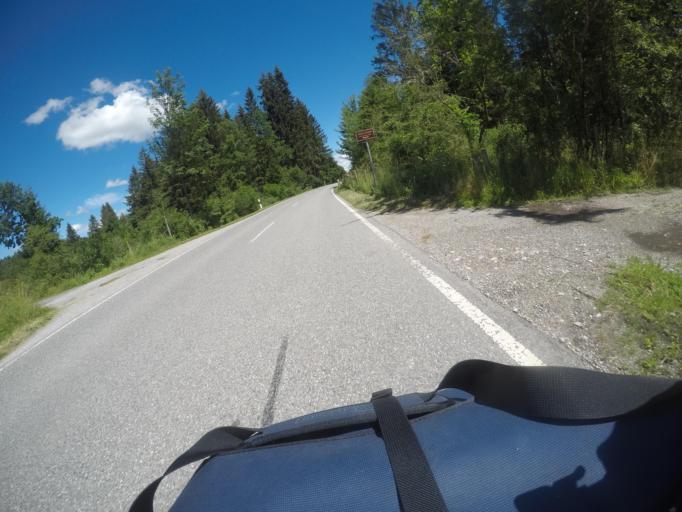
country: DE
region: Bavaria
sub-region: Upper Bavaria
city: Prem
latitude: 47.6624
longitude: 10.7846
